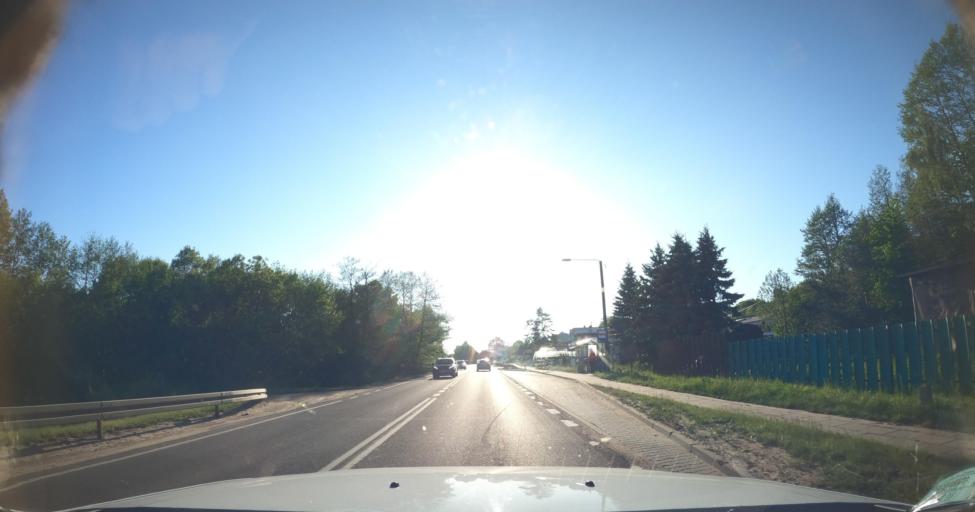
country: PL
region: Pomeranian Voivodeship
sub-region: Powiat kartuski
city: Zukowo
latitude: 54.3388
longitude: 18.3954
